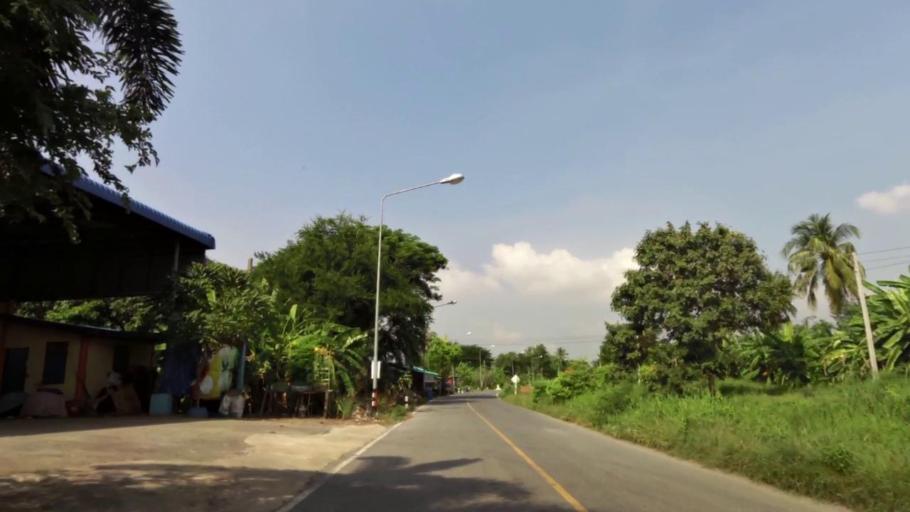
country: TH
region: Ang Thong
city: Ang Thong
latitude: 14.5999
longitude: 100.4006
